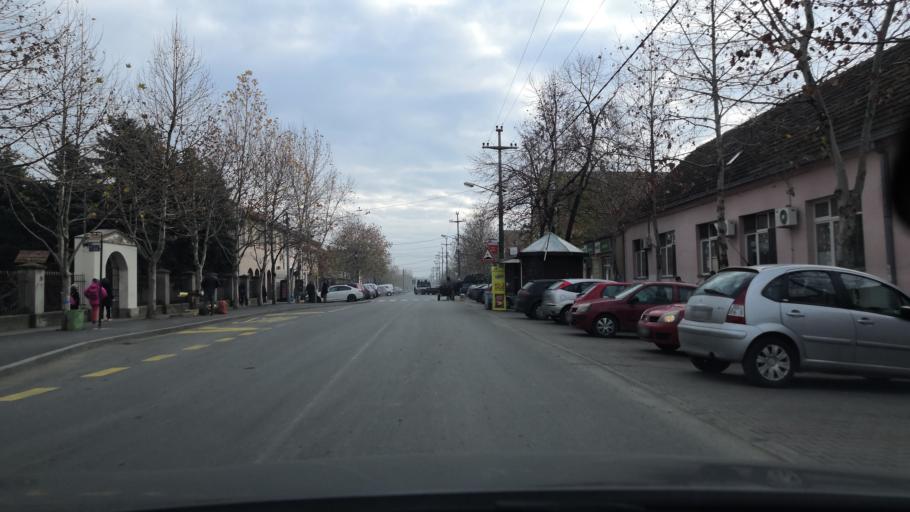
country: RS
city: Ugrinovci
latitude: 44.8758
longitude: 20.1868
